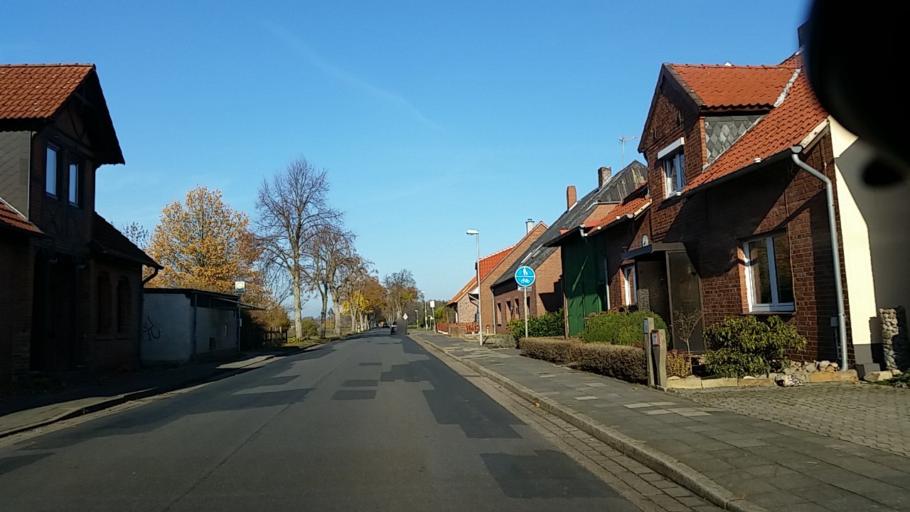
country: DE
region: Lower Saxony
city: Tulau
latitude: 52.5805
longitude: 10.8777
